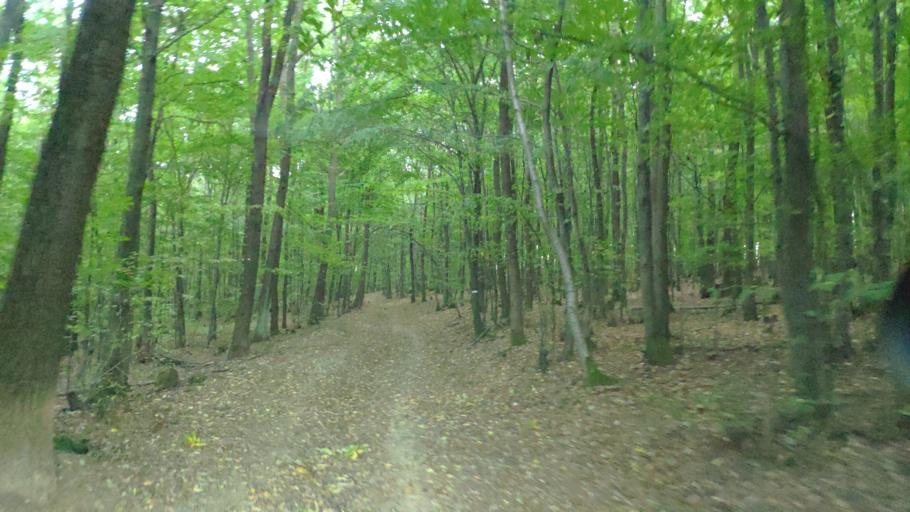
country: SK
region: Kosicky
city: Kosice
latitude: 48.6977
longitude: 21.1956
